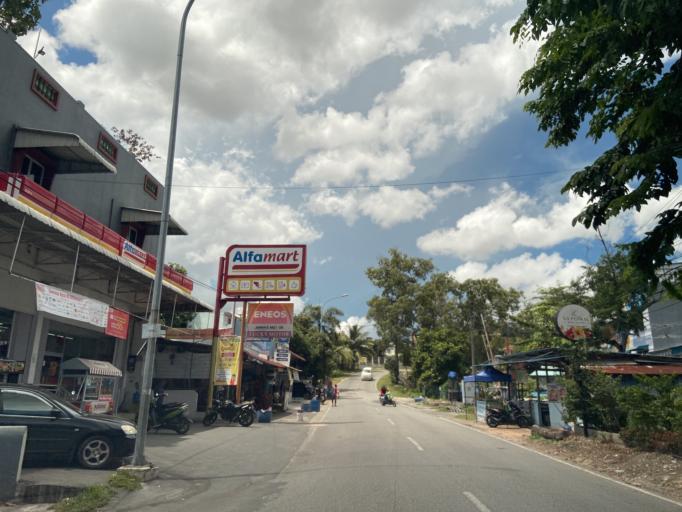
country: SG
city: Singapore
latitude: 1.1370
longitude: 104.0132
